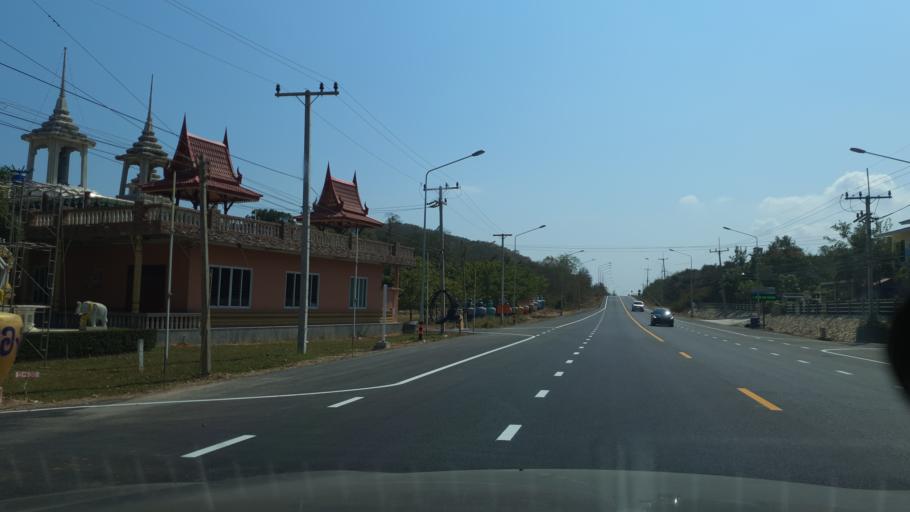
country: TH
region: Prachuap Khiri Khan
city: Sam Roi Yot
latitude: 12.2753
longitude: 99.9675
